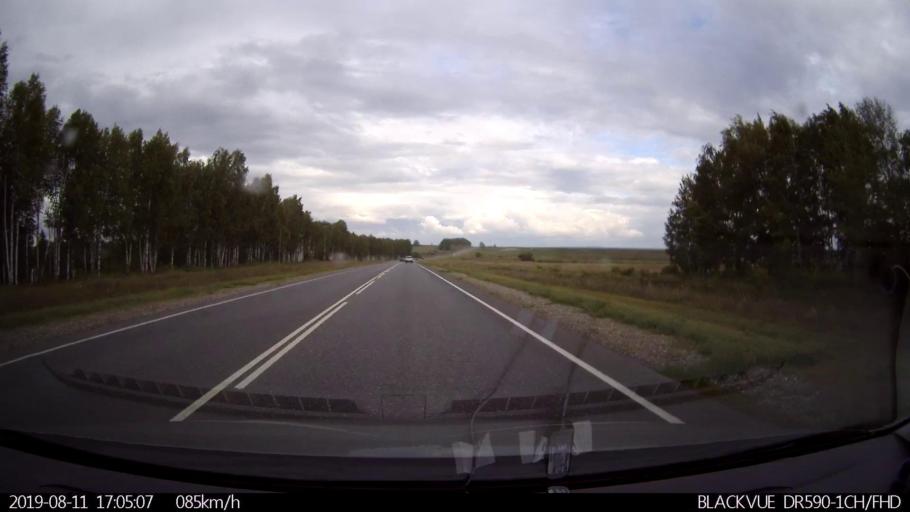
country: RU
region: Ulyanovsk
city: Mayna
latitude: 54.2994
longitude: 47.7790
